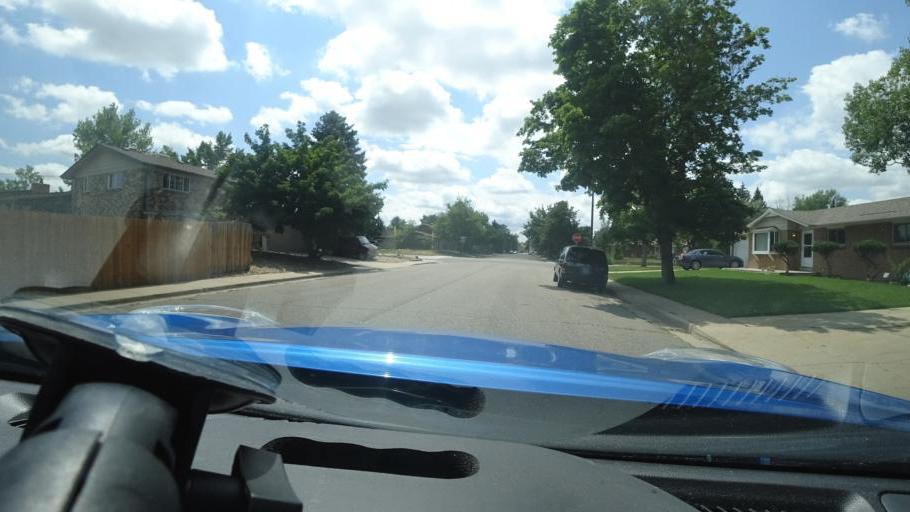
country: US
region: Colorado
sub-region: Adams County
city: Aurora
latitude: 39.7035
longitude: -104.8428
